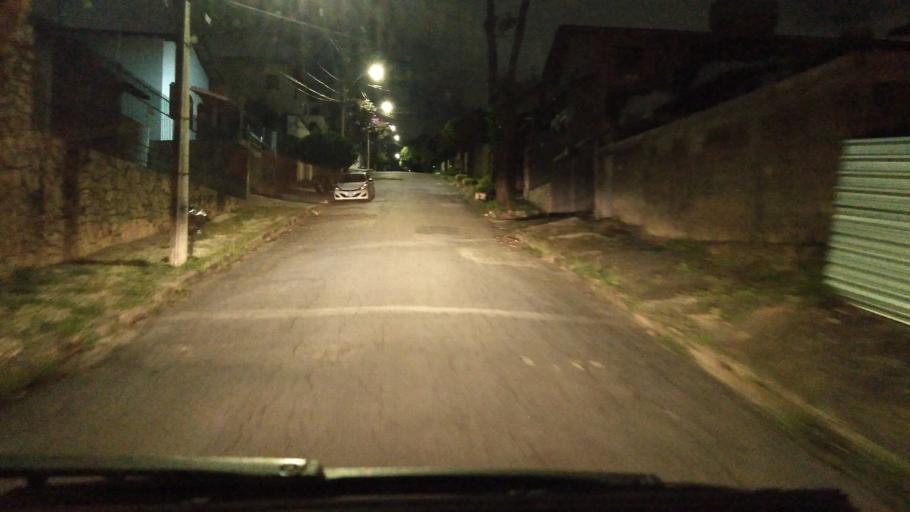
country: BR
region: Minas Gerais
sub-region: Belo Horizonte
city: Belo Horizonte
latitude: -19.8941
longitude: -43.9721
